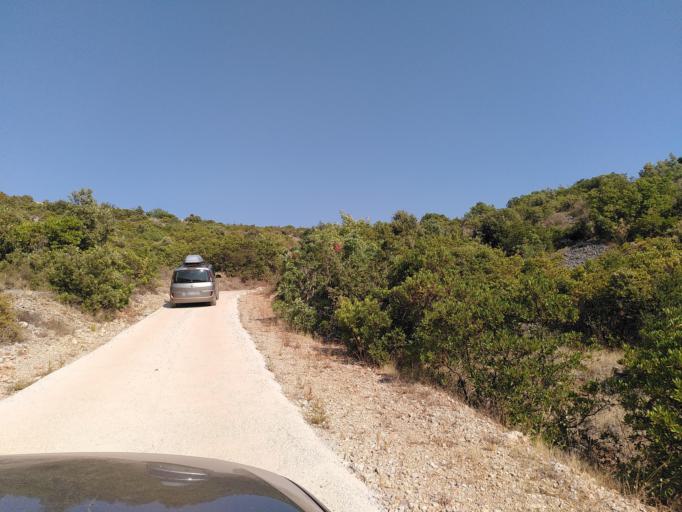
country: HR
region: Splitsko-Dalmatinska
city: Stari Grad
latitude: 43.1539
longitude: 16.5808
